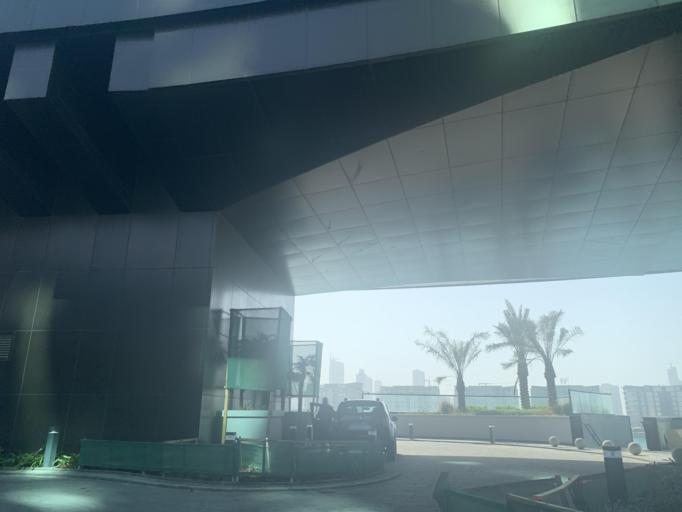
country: BH
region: Manama
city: Manama
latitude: 26.2412
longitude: 50.5726
